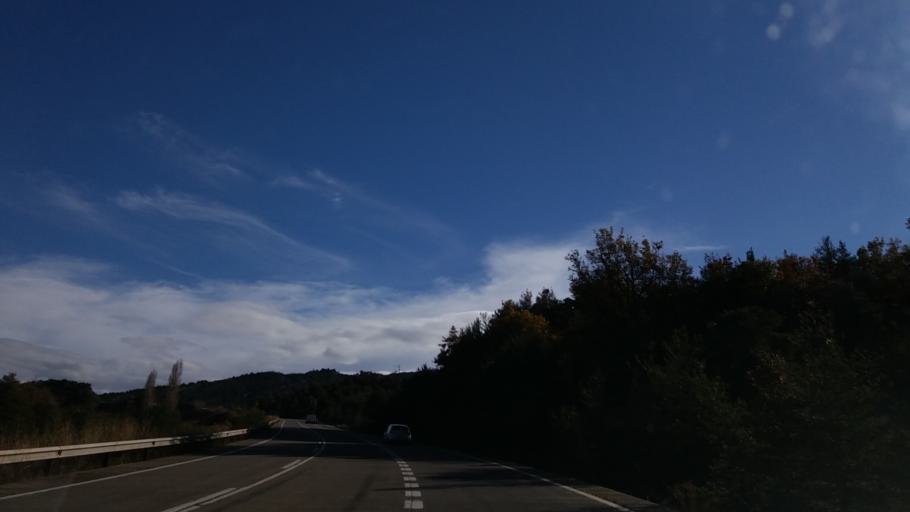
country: ES
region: Aragon
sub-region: Provincia de Huesca
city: Arguis
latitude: 42.3672
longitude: -0.3720
